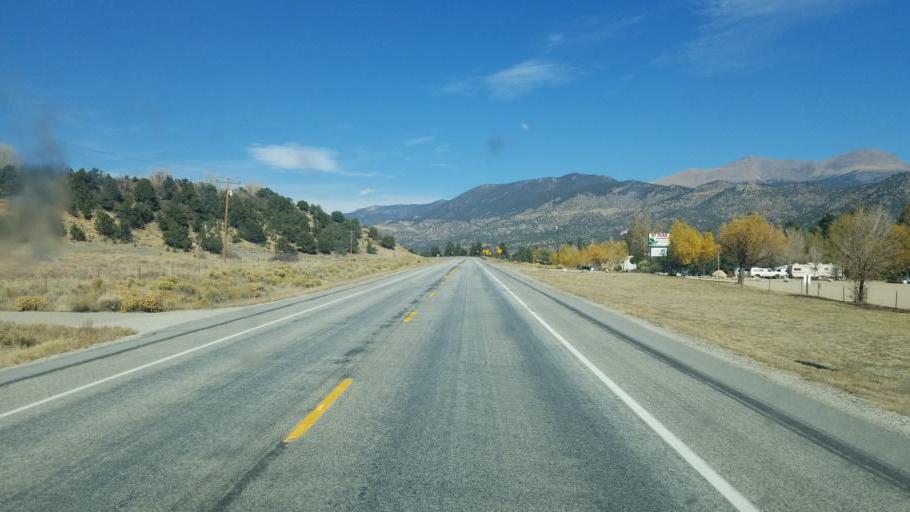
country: US
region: Colorado
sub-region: Chaffee County
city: Buena Vista
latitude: 38.8991
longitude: -106.1737
